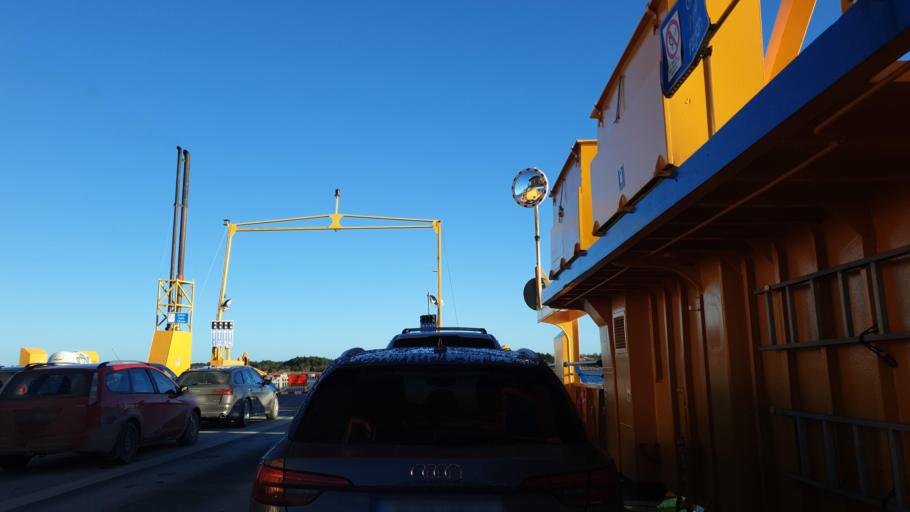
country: SE
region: Gotland
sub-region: Gotland
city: Slite
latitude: 57.8673
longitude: 19.0745
